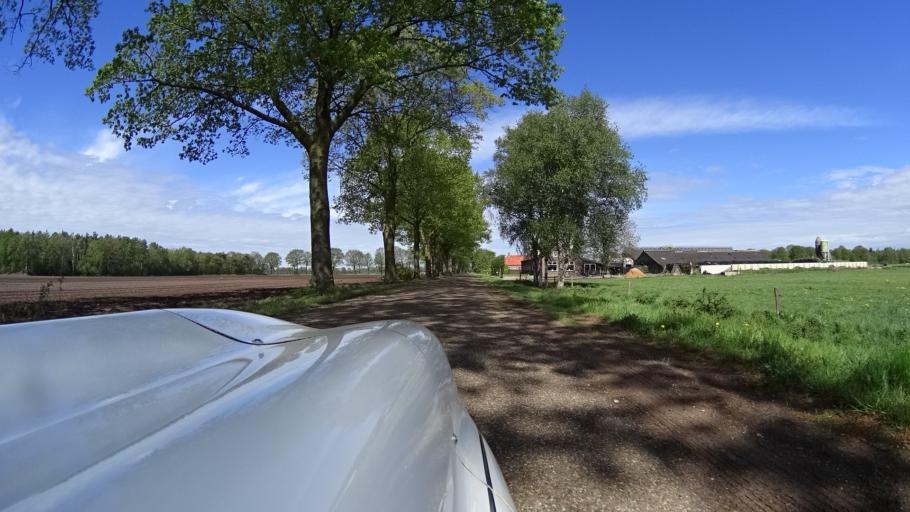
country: NL
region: North Brabant
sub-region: Gemeente Mill en Sint Hubert
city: Wilbertoord
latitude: 51.5987
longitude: 5.8073
